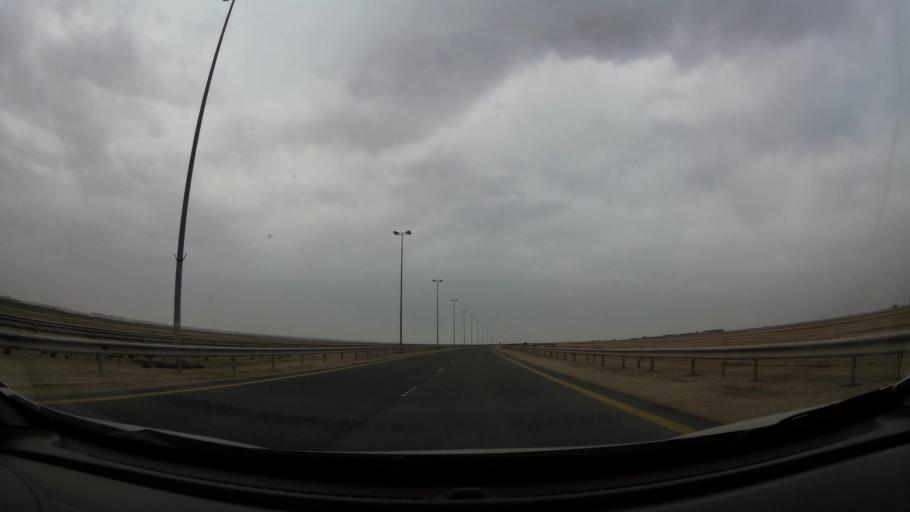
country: BH
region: Central Governorate
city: Dar Kulayb
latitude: 26.0098
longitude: 50.4837
